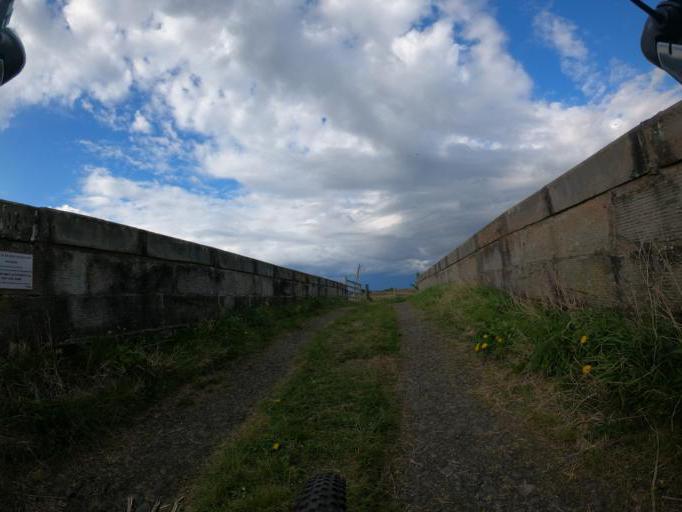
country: GB
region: Scotland
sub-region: Edinburgh
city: Currie
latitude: 55.9438
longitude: -3.3294
